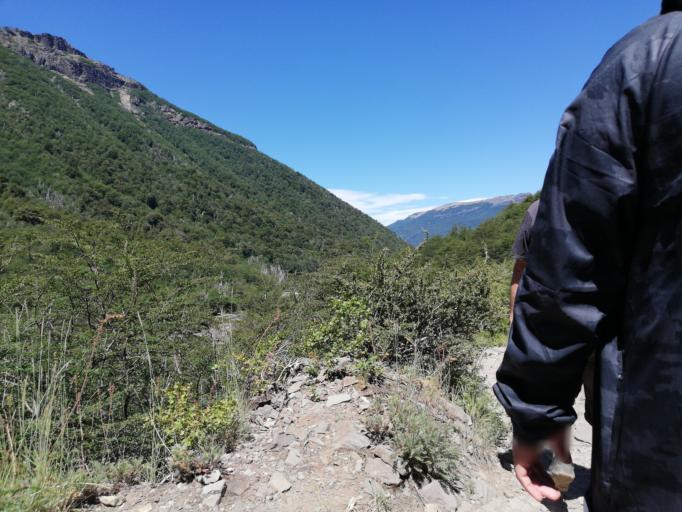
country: AR
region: Neuquen
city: Villa La Angostura
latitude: -41.1914
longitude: -71.8346
